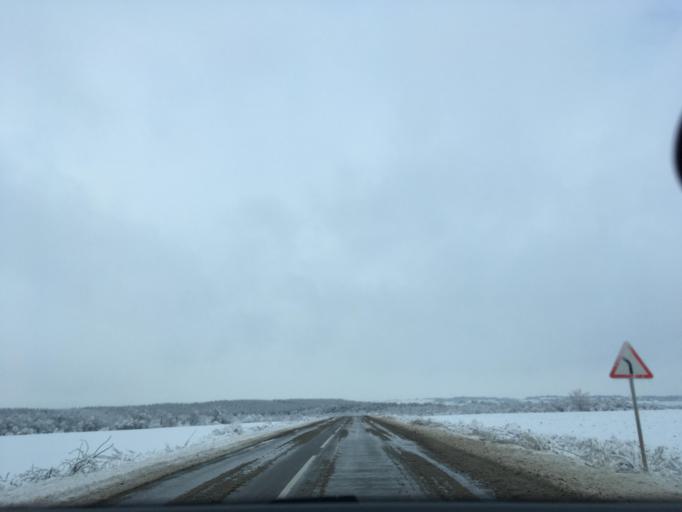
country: RU
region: Voronezj
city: Ol'khovatka
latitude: 50.1421
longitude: 39.2103
